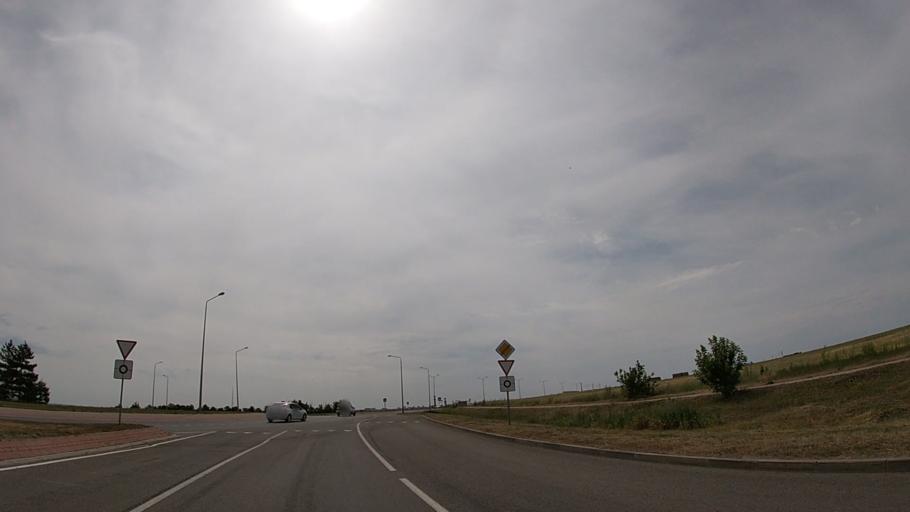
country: RU
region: Belgorod
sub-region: Belgorodskiy Rayon
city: Belgorod
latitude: 50.5933
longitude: 36.5297
